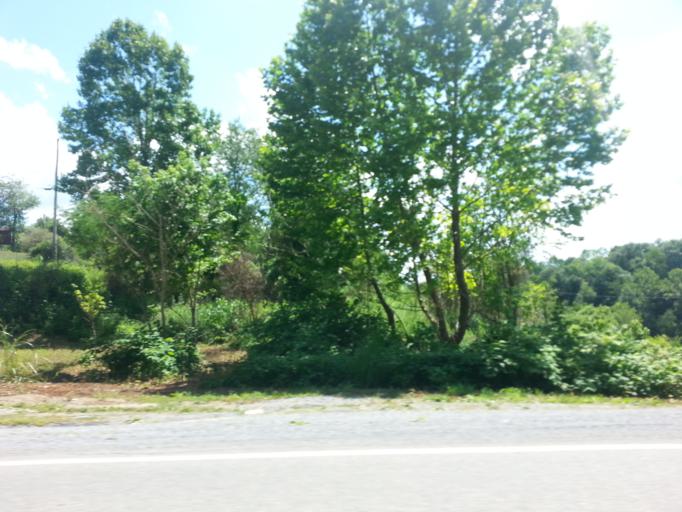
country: US
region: Virginia
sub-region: Lee County
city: Pennington Gap
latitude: 36.7327
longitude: -82.9968
